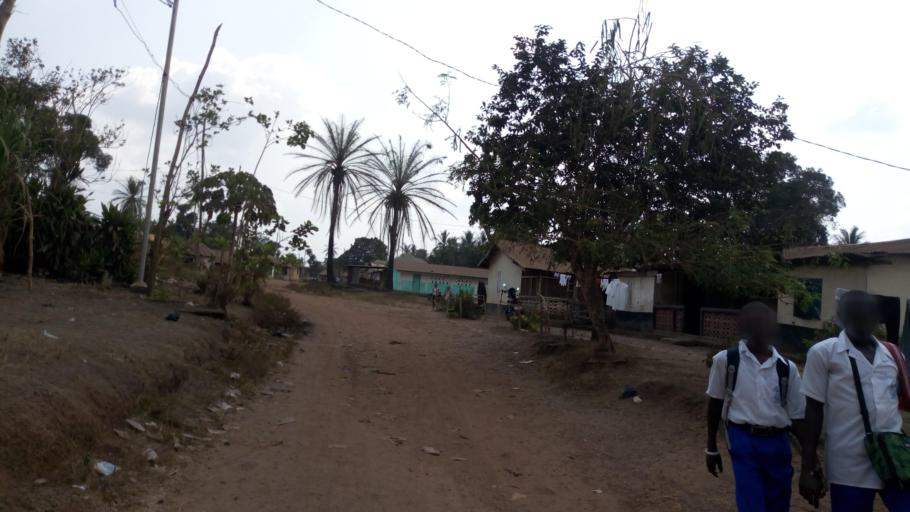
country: SL
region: Southern Province
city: Mogbwemo
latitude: 7.7900
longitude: -12.2984
